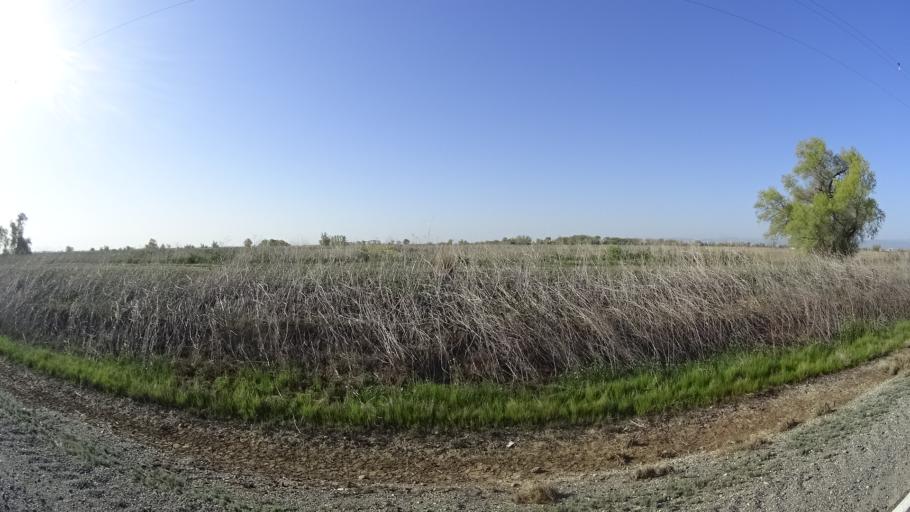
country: US
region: California
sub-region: Glenn County
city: Willows
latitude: 39.4072
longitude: -122.1698
